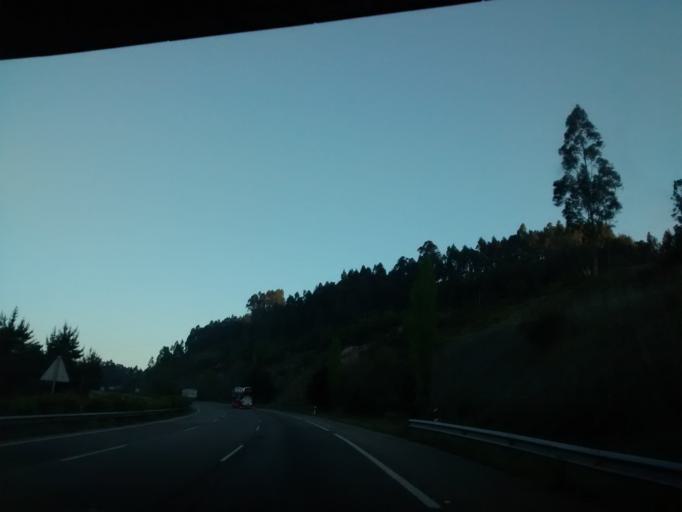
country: ES
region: Asturias
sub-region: Province of Asturias
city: Colunga
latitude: 43.4917
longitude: -5.3205
